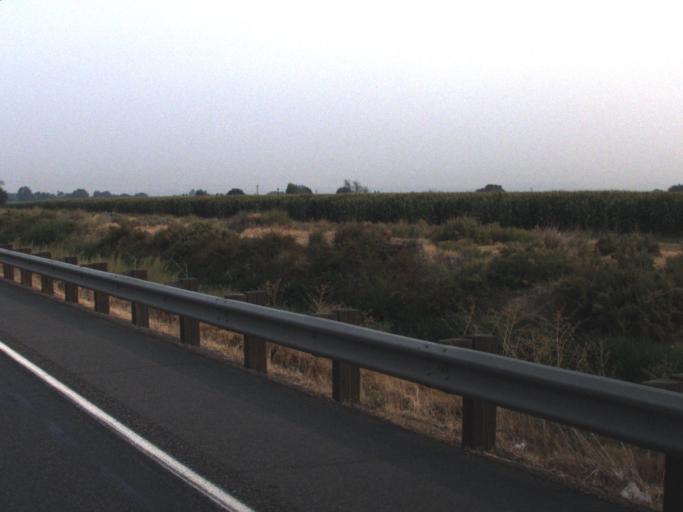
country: US
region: Washington
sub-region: Yakima County
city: Toppenish
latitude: 46.3422
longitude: -120.3205
